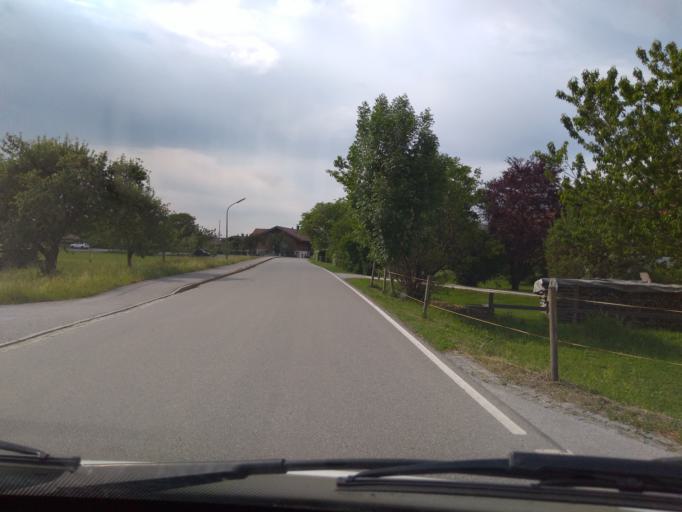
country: DE
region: Bavaria
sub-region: Upper Bavaria
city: Nussdorf am Inn
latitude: 47.7392
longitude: 12.1567
